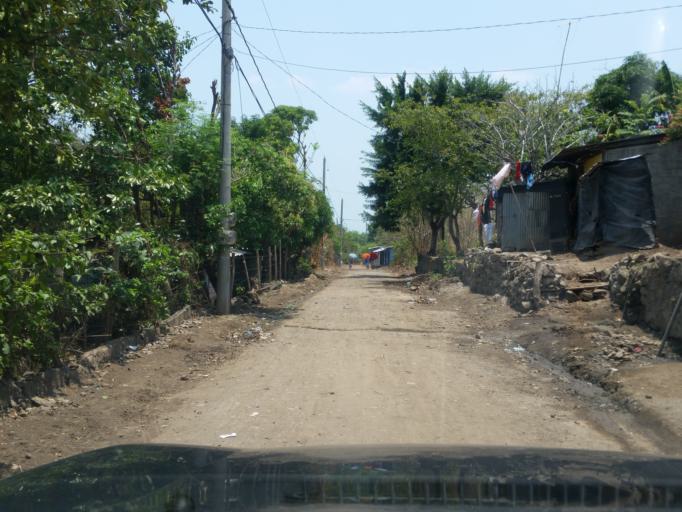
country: NI
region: Granada
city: Granada
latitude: 11.9080
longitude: -85.9483
